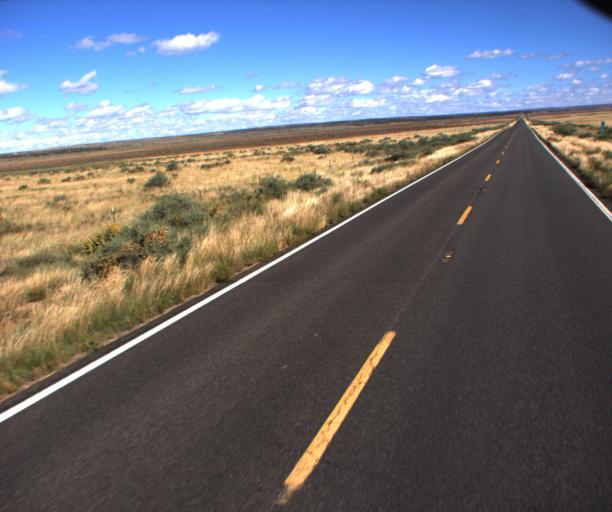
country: US
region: Arizona
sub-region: Apache County
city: Saint Johns
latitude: 34.6817
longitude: -109.2817
